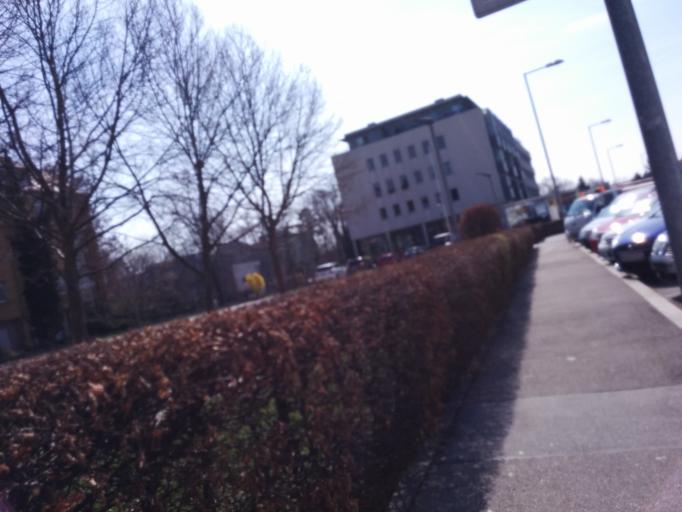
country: AT
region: Lower Austria
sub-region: Politischer Bezirk Baden
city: Baden
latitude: 48.0049
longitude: 16.2318
